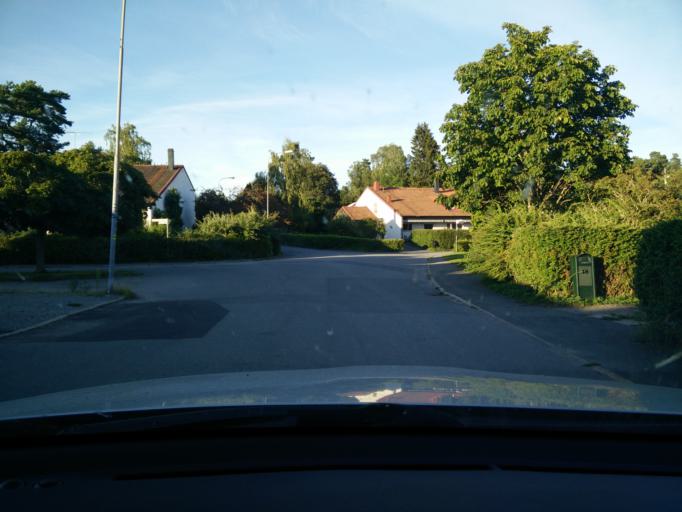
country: SE
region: Stockholm
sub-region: Sollentuna Kommun
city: Sollentuna
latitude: 59.4517
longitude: 17.9569
